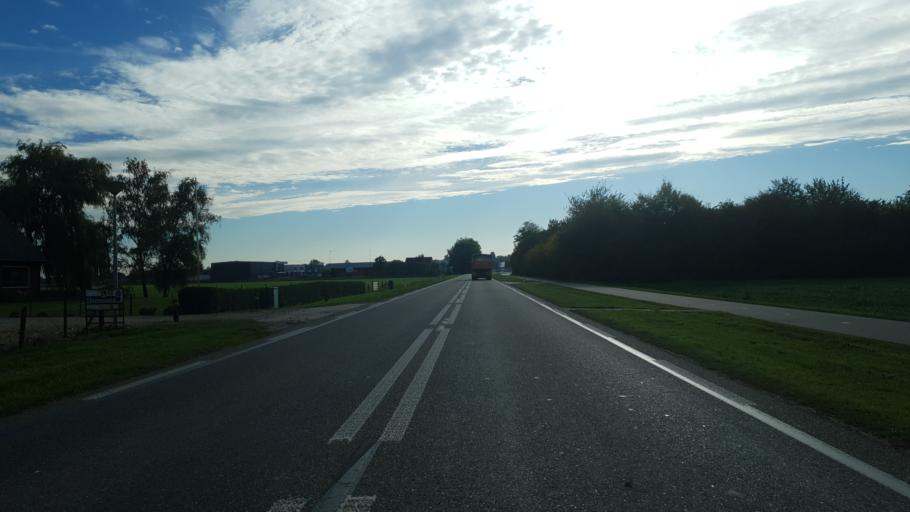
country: DE
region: North Rhine-Westphalia
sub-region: Regierungsbezirk Dusseldorf
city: Kranenburg
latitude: 51.8449
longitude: 6.0023
